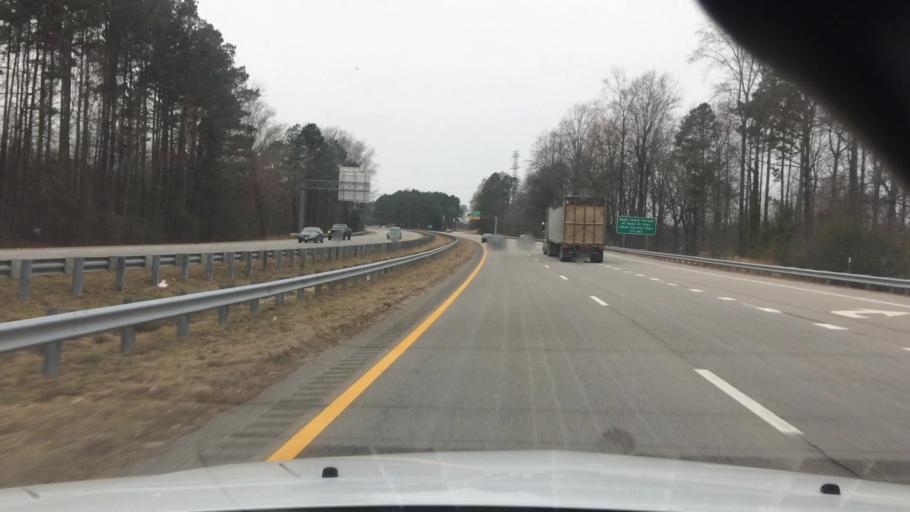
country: US
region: North Carolina
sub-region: Nash County
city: Red Oak
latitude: 35.9827
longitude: -77.8904
